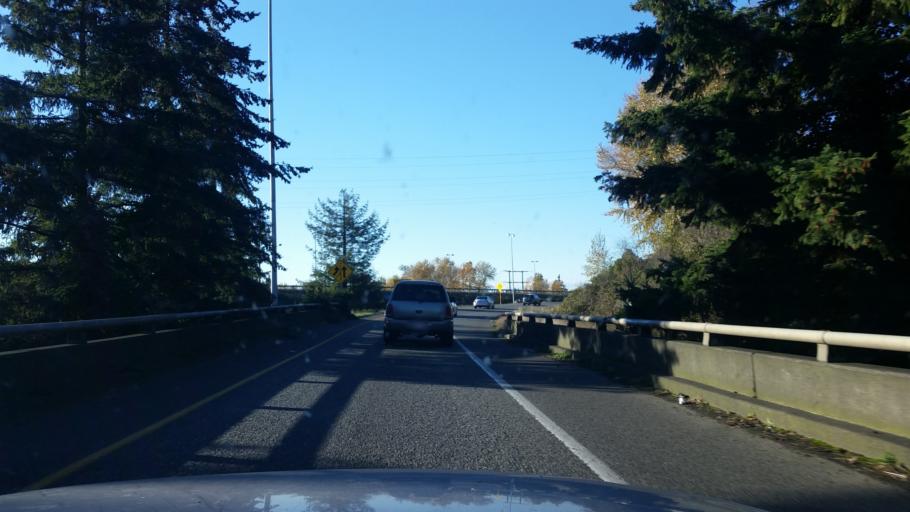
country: US
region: Washington
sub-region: King County
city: Newport
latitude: 47.5812
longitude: -122.1725
